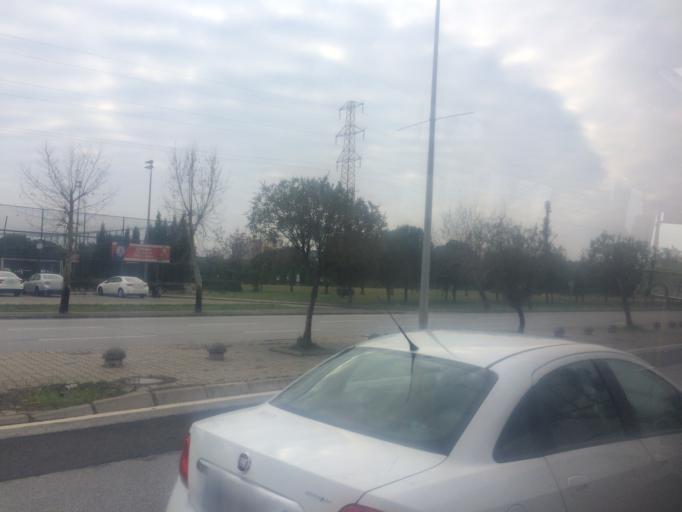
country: TR
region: Izmir
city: Karsiyaka
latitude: 38.4939
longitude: 27.0394
